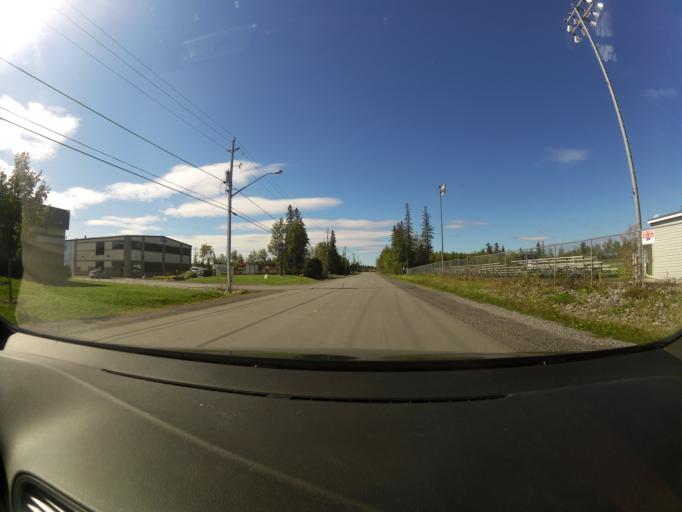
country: CA
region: Ontario
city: Bells Corners
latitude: 45.2706
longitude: -75.9582
